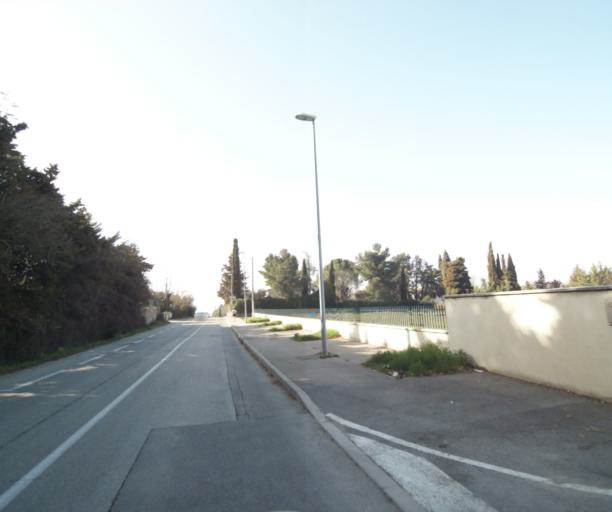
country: FR
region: Provence-Alpes-Cote d'Azur
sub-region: Departement des Bouches-du-Rhone
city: Aix-en-Provence
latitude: 43.5500
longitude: 5.4565
